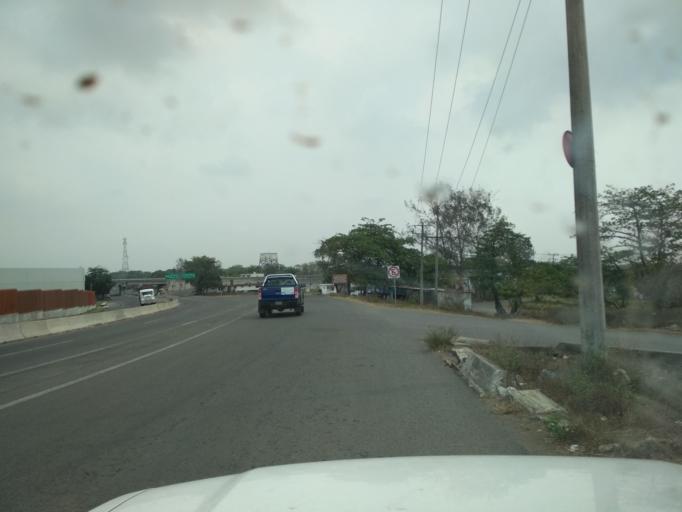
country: MX
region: Veracruz
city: Paso del Toro
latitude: 19.0206
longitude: -96.1350
